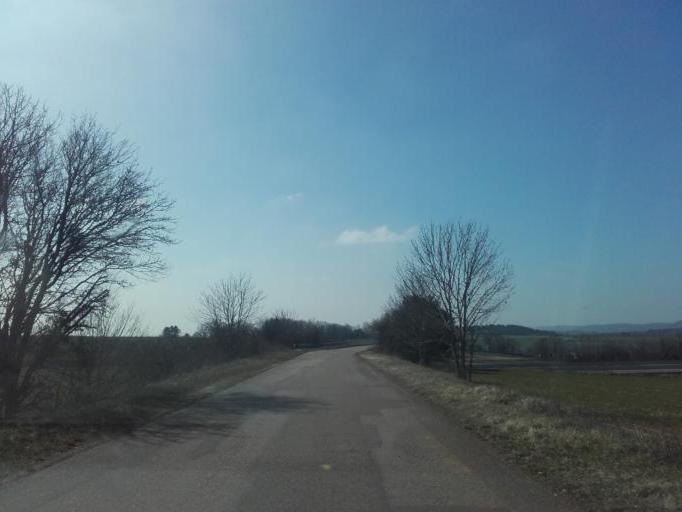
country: FR
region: Bourgogne
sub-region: Departement de la Cote-d'Or
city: Savigny-les-Beaune
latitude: 47.0601
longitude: 4.7786
